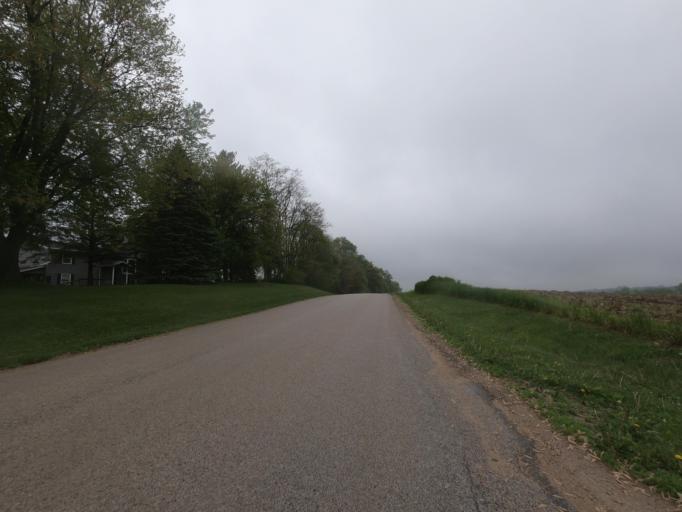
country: US
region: Wisconsin
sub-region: Grant County
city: Hazel Green
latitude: 42.4897
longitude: -90.4935
